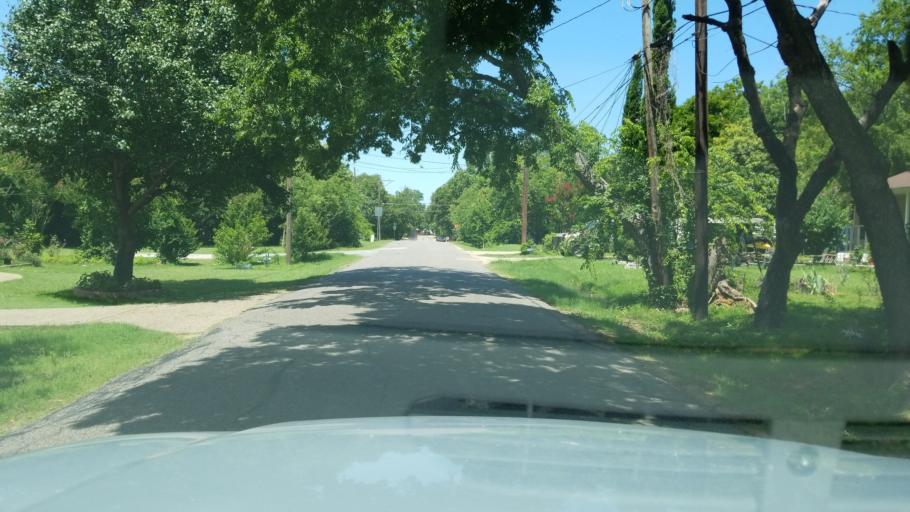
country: US
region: Texas
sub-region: Dallas County
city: Irving
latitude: 32.8036
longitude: -96.9285
